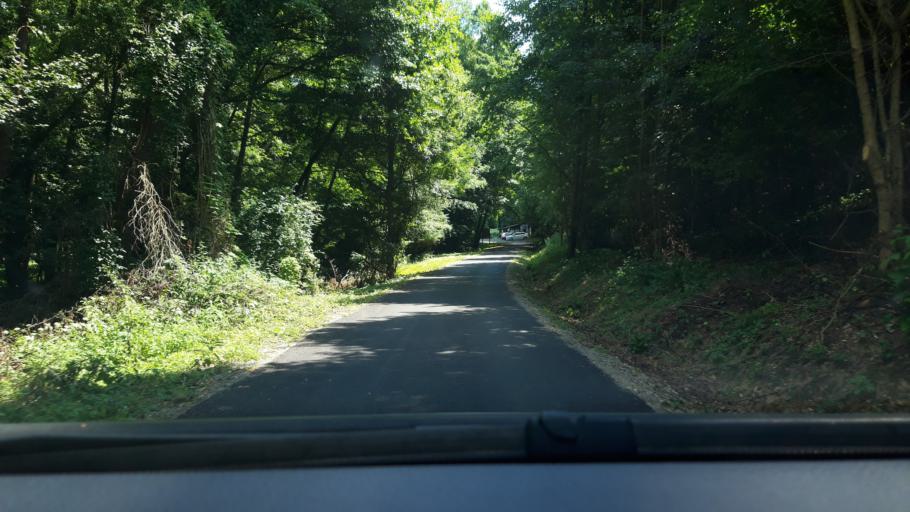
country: HU
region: Nograd
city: Somoskoujfalu
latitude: 48.1799
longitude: 19.8532
